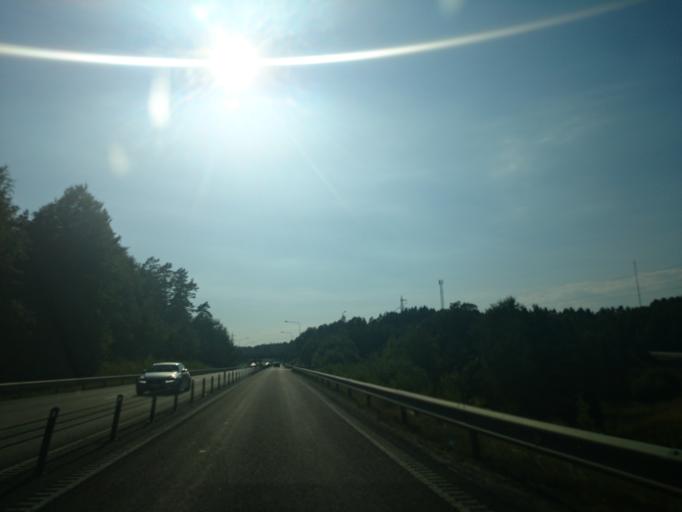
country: SE
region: Blekinge
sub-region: Karlshamns Kommun
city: Karlshamn
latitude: 56.1888
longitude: 14.9326
